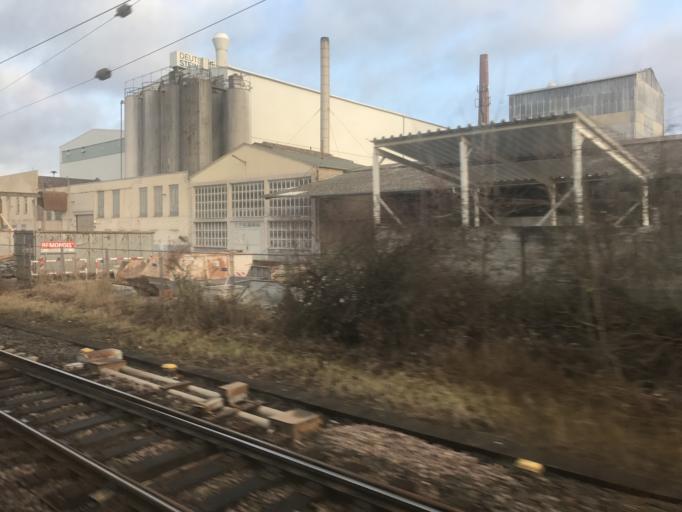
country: DE
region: Rheinland-Pfalz
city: Sinzig
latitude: 50.5439
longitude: 7.2609
